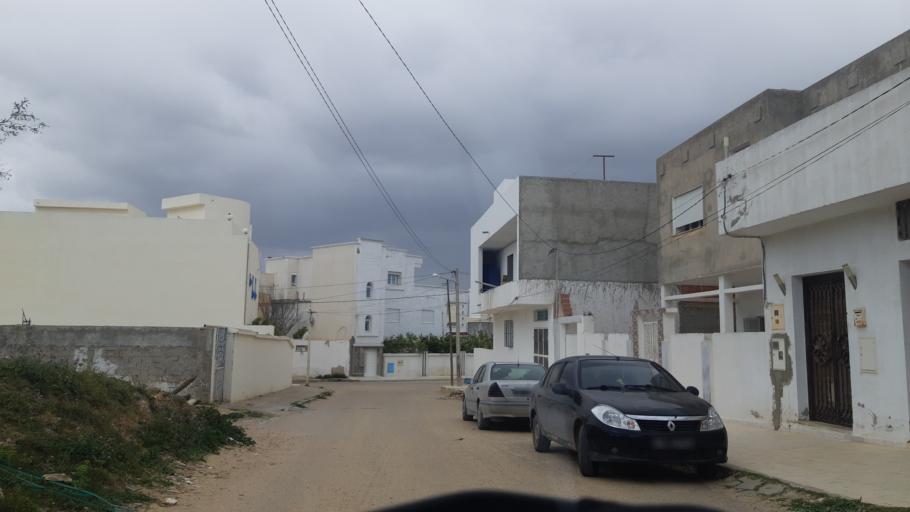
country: TN
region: Susah
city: Akouda
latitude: 35.8665
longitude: 10.5509
